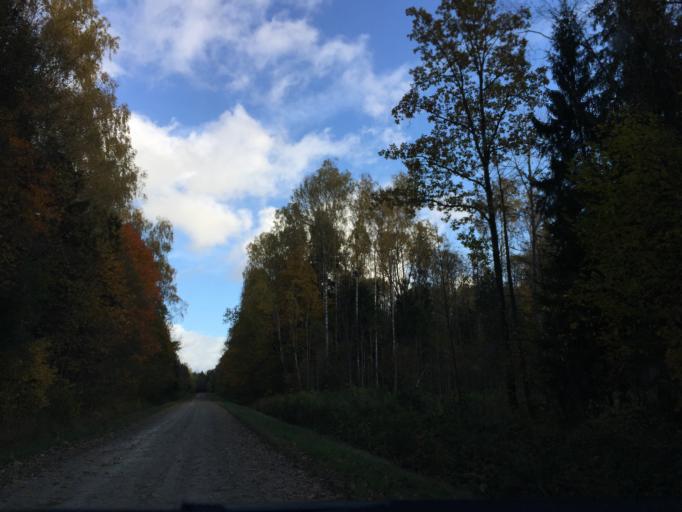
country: LV
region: Ogre
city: Jumprava
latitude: 56.7398
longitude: 24.9444
